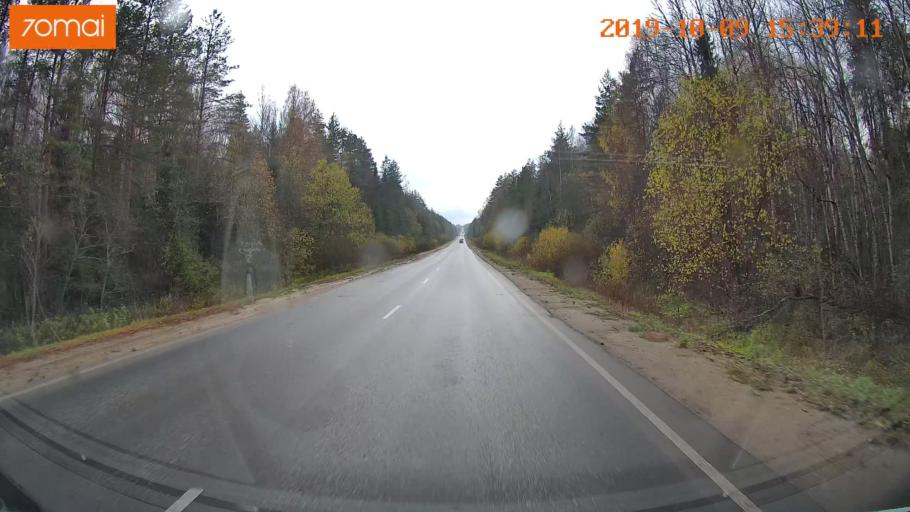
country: RU
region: Kostroma
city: Oktyabr'skiy
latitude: 57.8995
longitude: 41.1698
